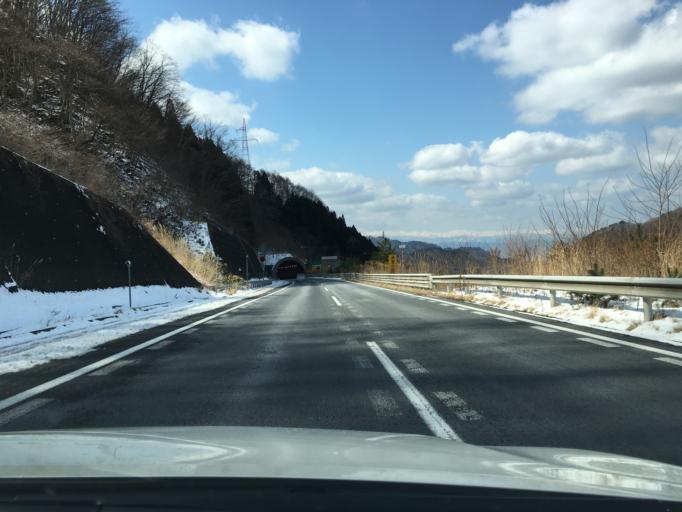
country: JP
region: Yamagata
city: Yamagata-shi
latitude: 38.2239
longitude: 140.4420
